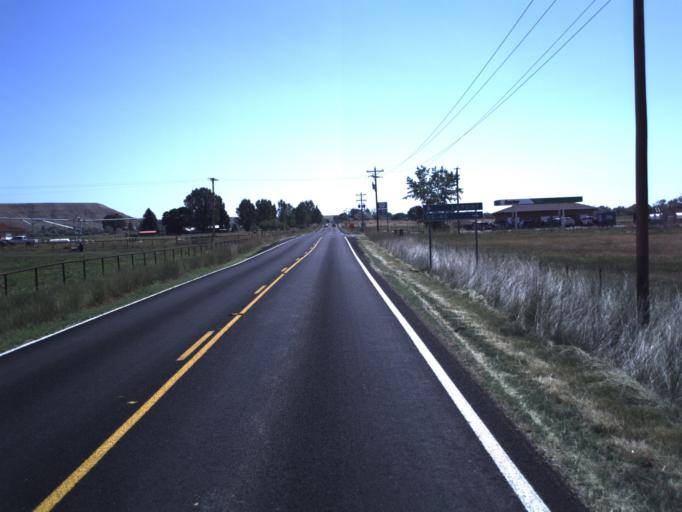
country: US
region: Utah
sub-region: Duchesne County
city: Roosevelt
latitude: 40.4037
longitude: -109.8233
